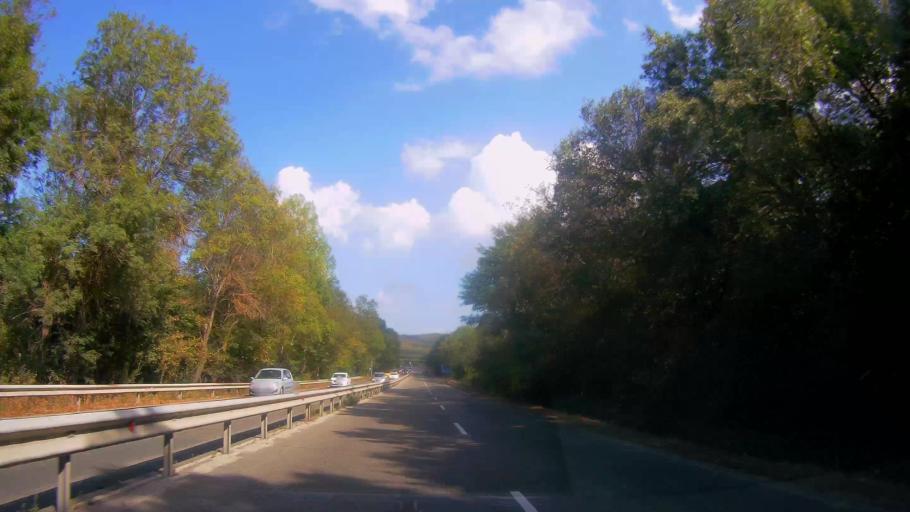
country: BG
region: Burgas
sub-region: Obshtina Sozopol
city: Chernomorets
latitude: 42.4287
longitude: 27.5410
